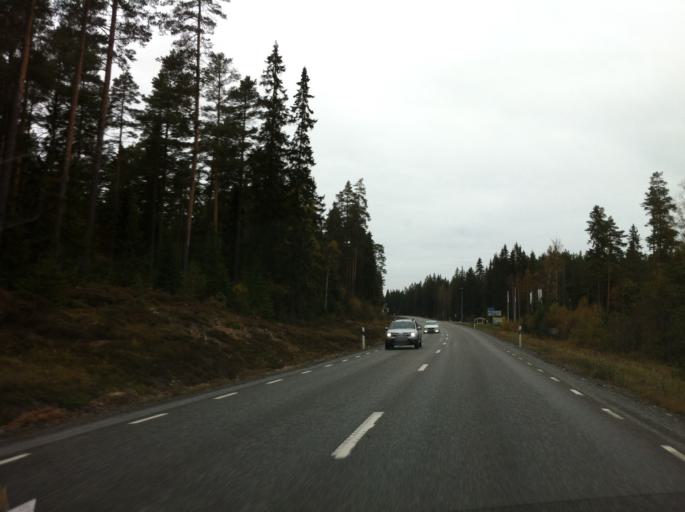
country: SE
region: OErebro
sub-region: Ljusnarsbergs Kommun
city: Kopparberg
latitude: 59.9073
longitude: 15.0214
